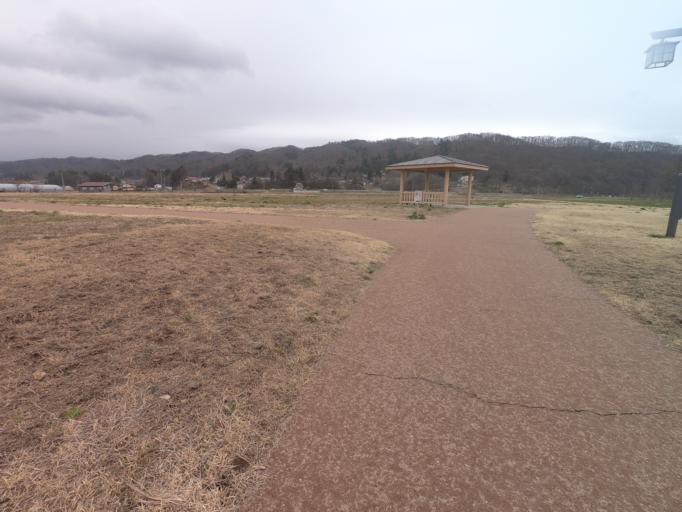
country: JP
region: Iwate
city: Kitakami
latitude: 39.2794
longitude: 141.1287
